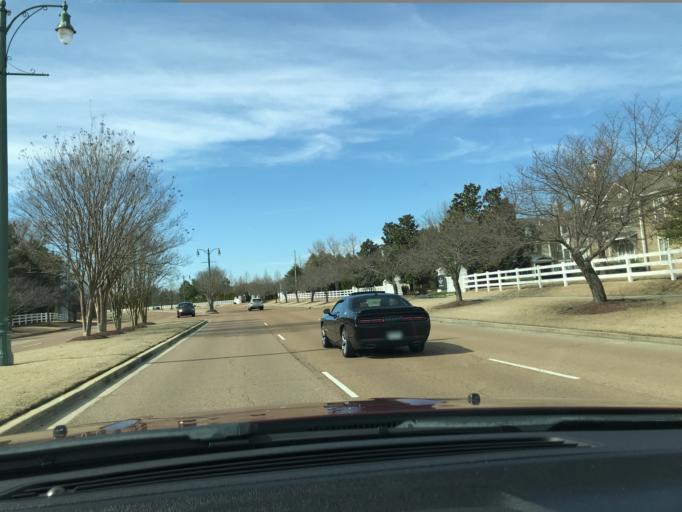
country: US
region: Tennessee
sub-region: Shelby County
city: Collierville
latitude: 35.0396
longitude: -89.7094
